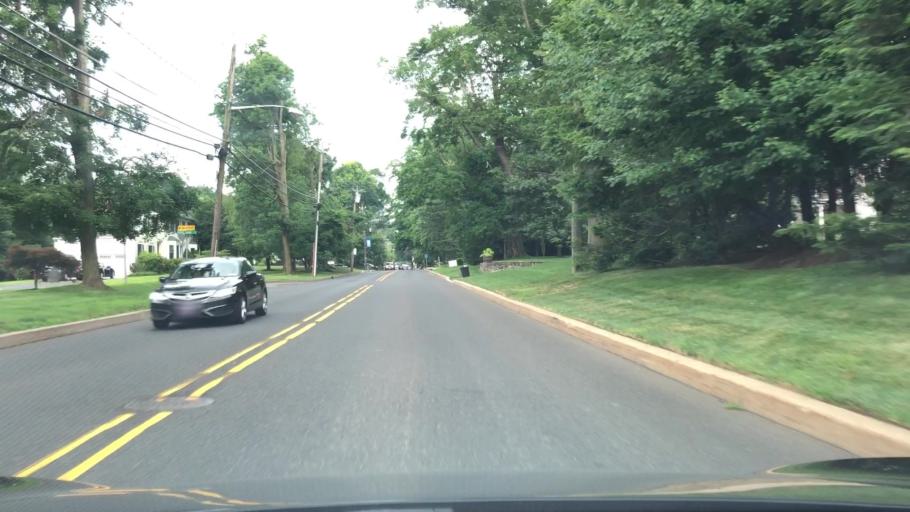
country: US
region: New Jersey
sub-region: Mercer County
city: Pennington
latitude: 40.3287
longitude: -74.7850
